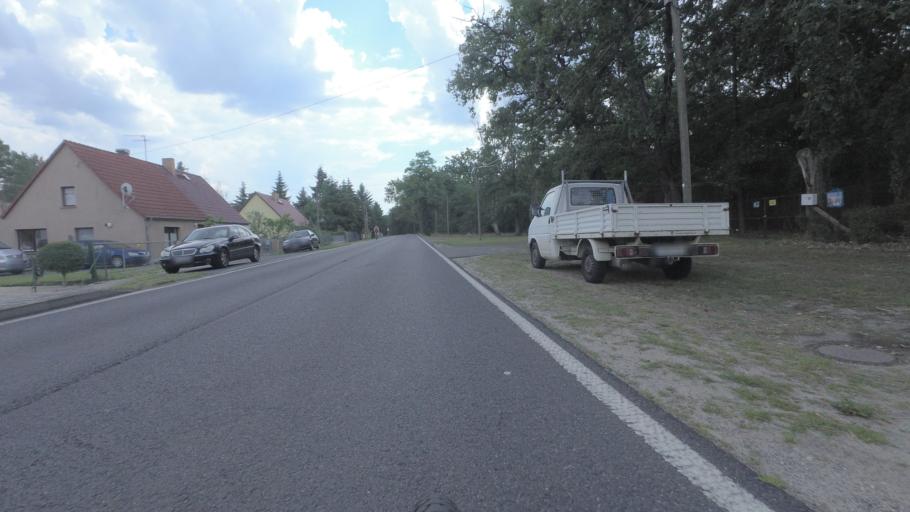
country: DE
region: Brandenburg
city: Sperenberg
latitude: 52.1641
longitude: 13.3264
